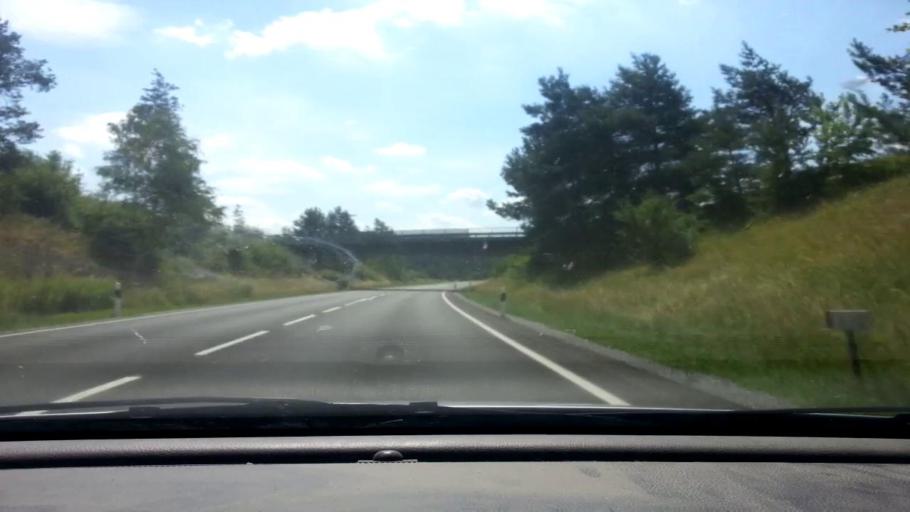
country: DE
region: Bavaria
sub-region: Upper Franconia
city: Seybothenreuth
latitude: 49.8949
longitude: 11.7130
